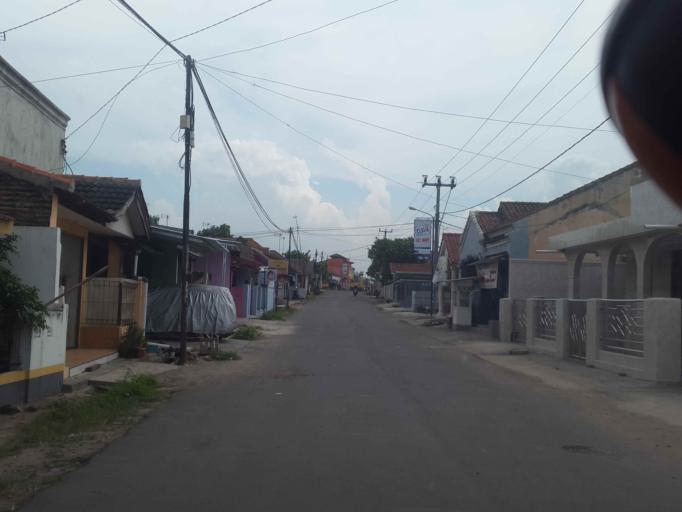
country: ID
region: Banten
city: Curug
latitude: -6.0225
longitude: 106.0612
